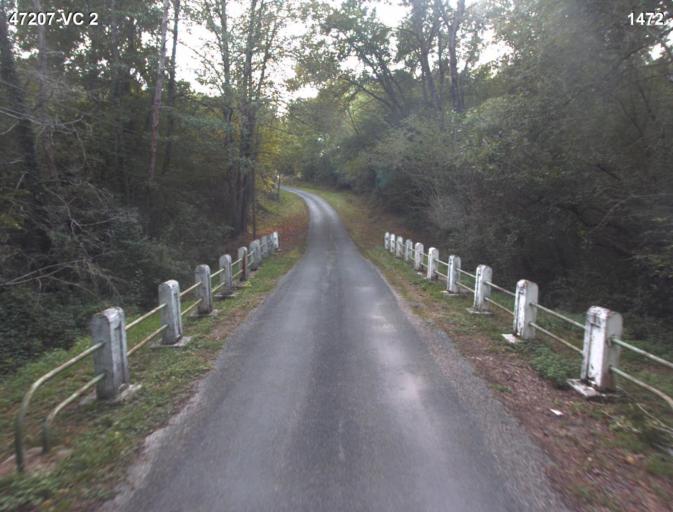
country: FR
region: Aquitaine
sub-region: Departement du Lot-et-Garonne
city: Barbaste
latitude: 44.1896
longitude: 0.2290
